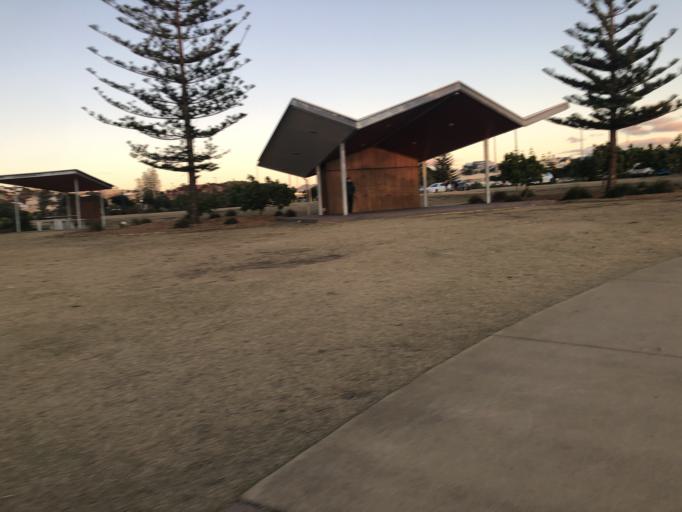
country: AU
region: New South Wales
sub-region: Coffs Harbour
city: Coffs Harbour
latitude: -30.3032
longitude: 153.1408
